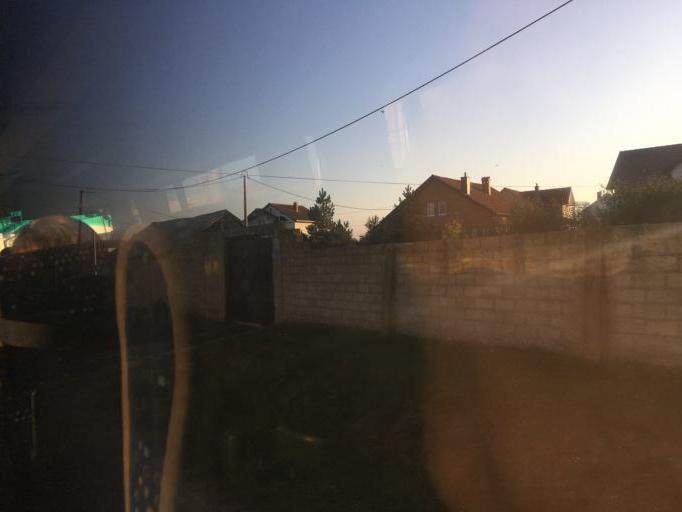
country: XK
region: Pristina
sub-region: Komuna e Drenasit
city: Glogovac
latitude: 42.5948
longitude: 20.8924
